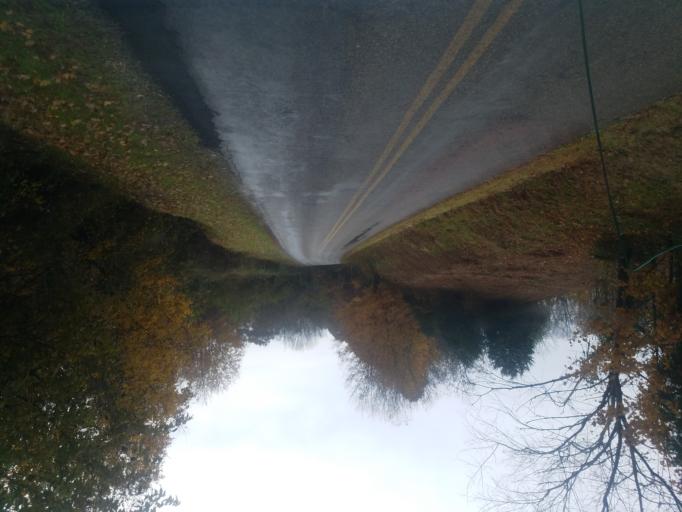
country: US
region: Ohio
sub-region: Washington County
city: Beverly
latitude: 39.5520
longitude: -81.6738
